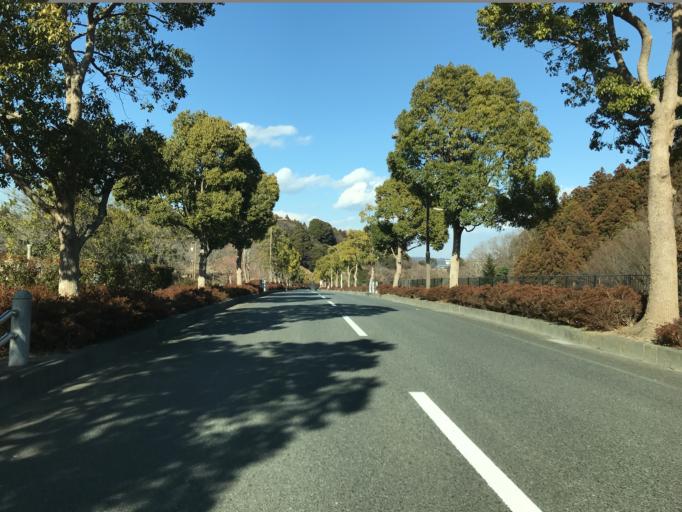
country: JP
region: Fukushima
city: Iwaki
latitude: 37.0319
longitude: 140.8986
